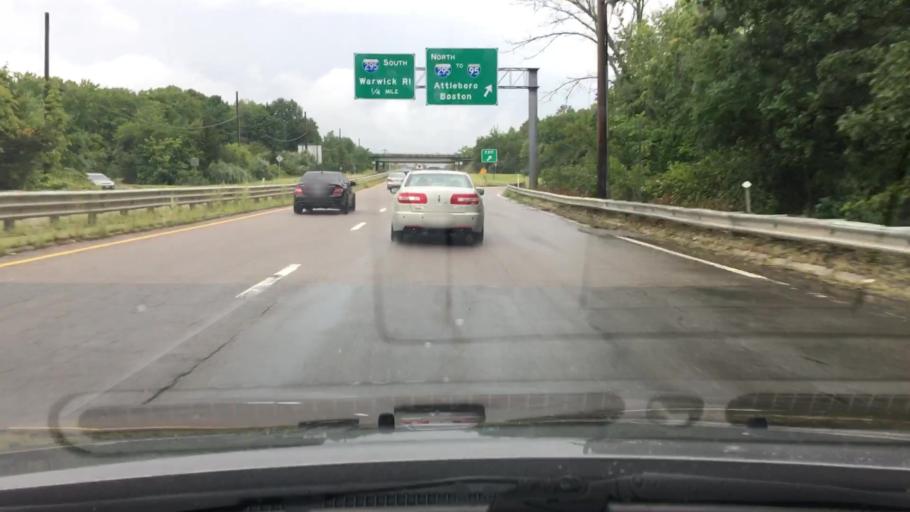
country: US
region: Rhode Island
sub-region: Providence County
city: Valley Falls
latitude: 41.9463
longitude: -71.3469
